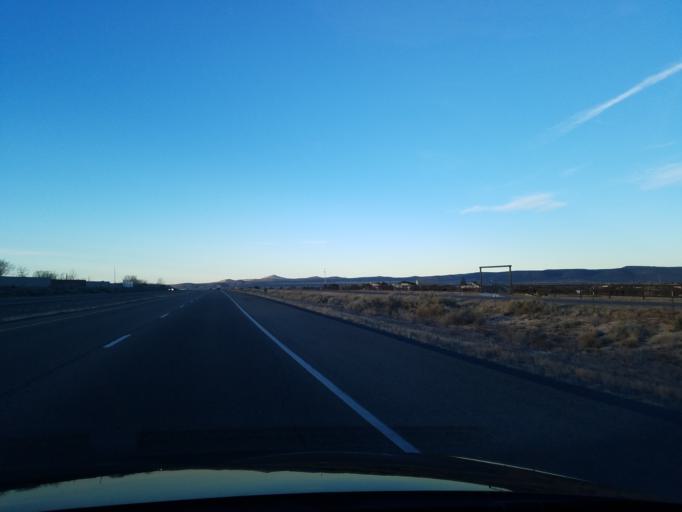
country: US
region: New Mexico
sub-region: Santa Fe County
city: Agua Fria
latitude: 35.6529
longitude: -106.0436
